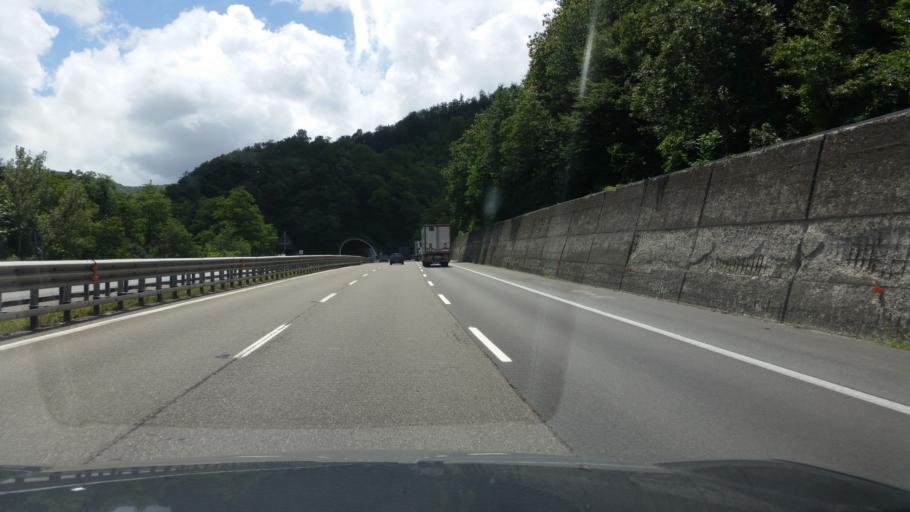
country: IT
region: Liguria
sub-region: Provincia di Genova
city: Campo Ligure
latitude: 44.5328
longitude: 8.6970
